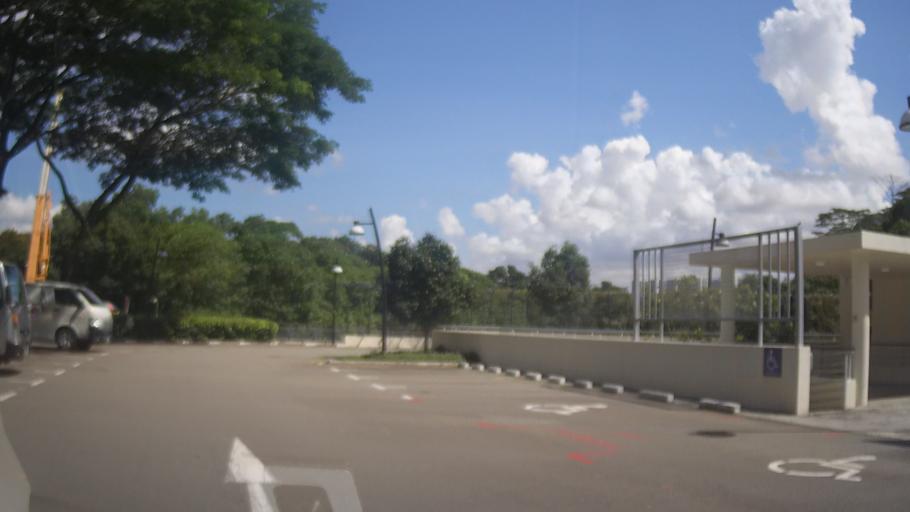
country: MY
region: Johor
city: Johor Bahru
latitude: 1.4437
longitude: 103.7817
